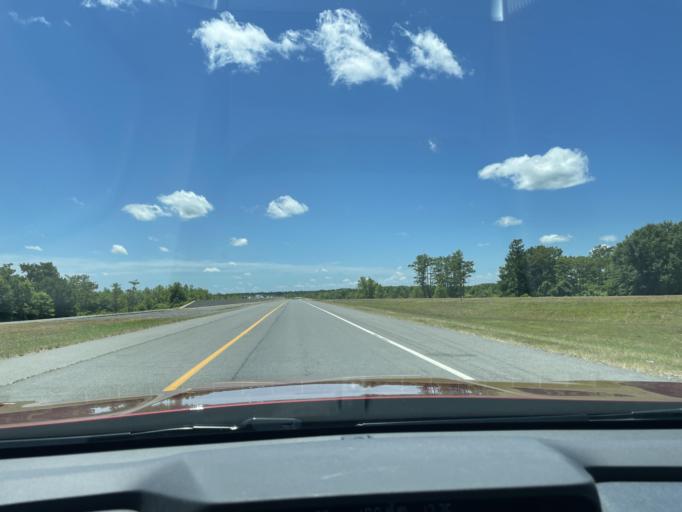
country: US
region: Arkansas
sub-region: Jefferson County
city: Pine Bluff
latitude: 34.1698
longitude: -91.9861
